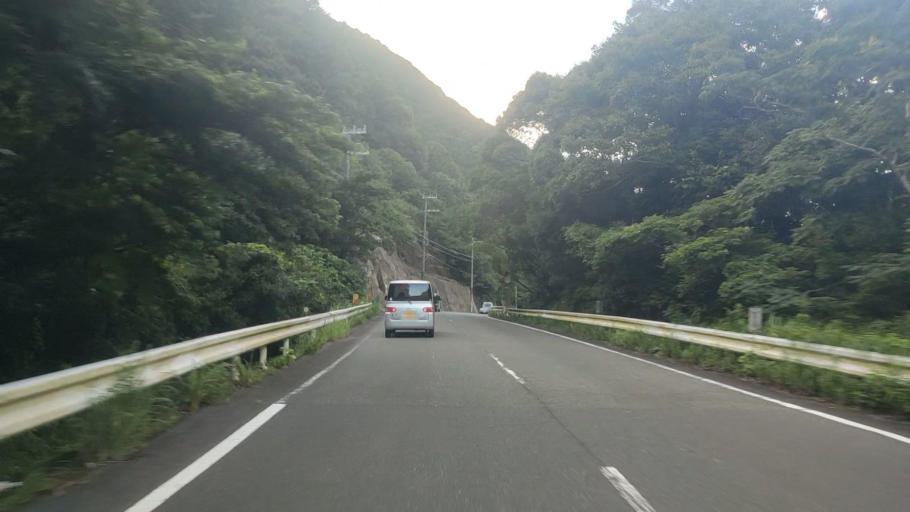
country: JP
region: Wakayama
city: Tanabe
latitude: 33.7659
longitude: 135.5000
